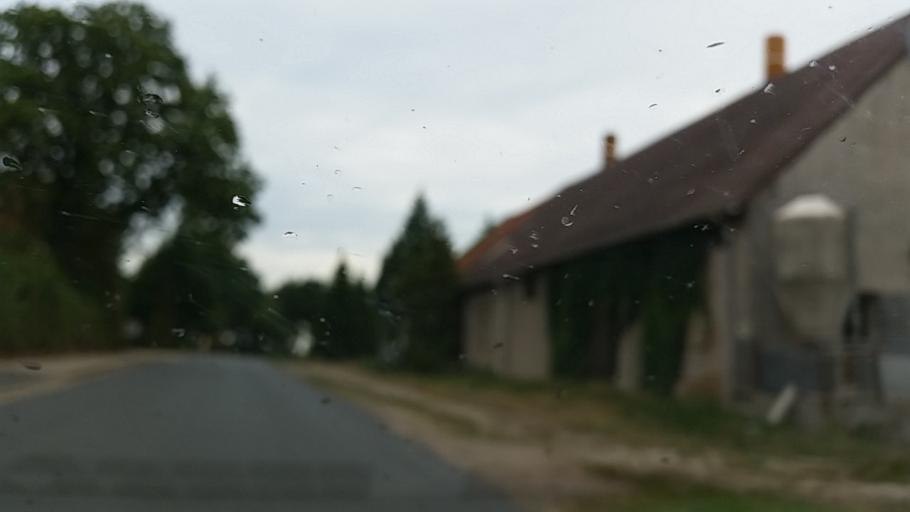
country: DE
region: Lower Saxony
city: Gilten
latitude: 52.6947
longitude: 9.5986
